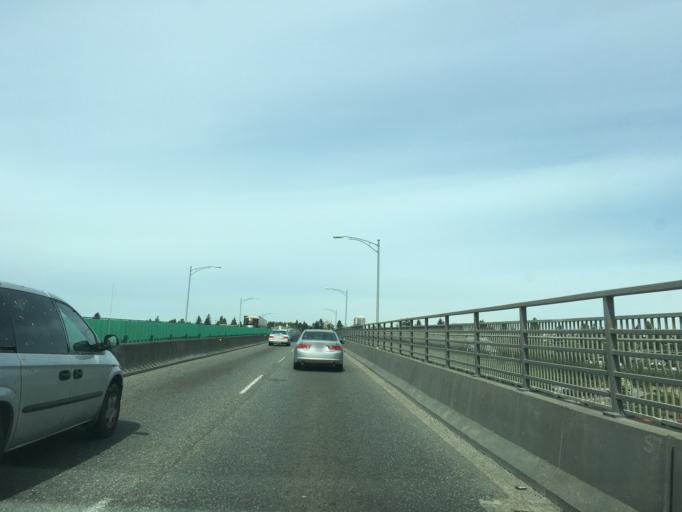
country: CA
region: British Columbia
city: New Westminster
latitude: 49.1949
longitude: -122.9454
